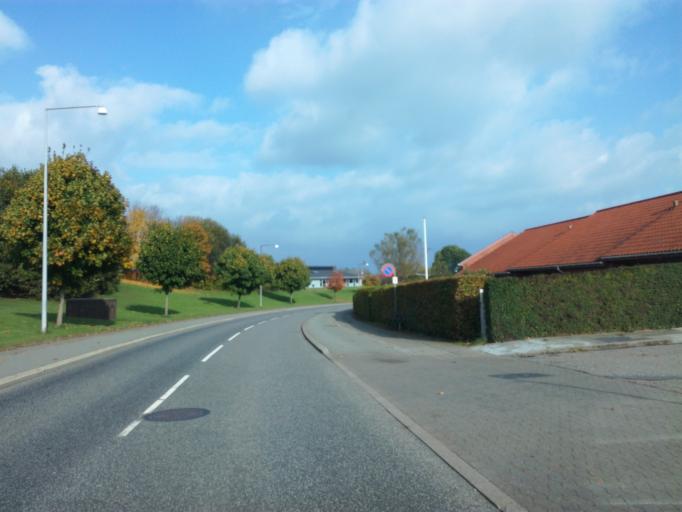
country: DK
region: South Denmark
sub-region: Vejle Kommune
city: Borkop
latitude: 55.6401
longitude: 9.6441
